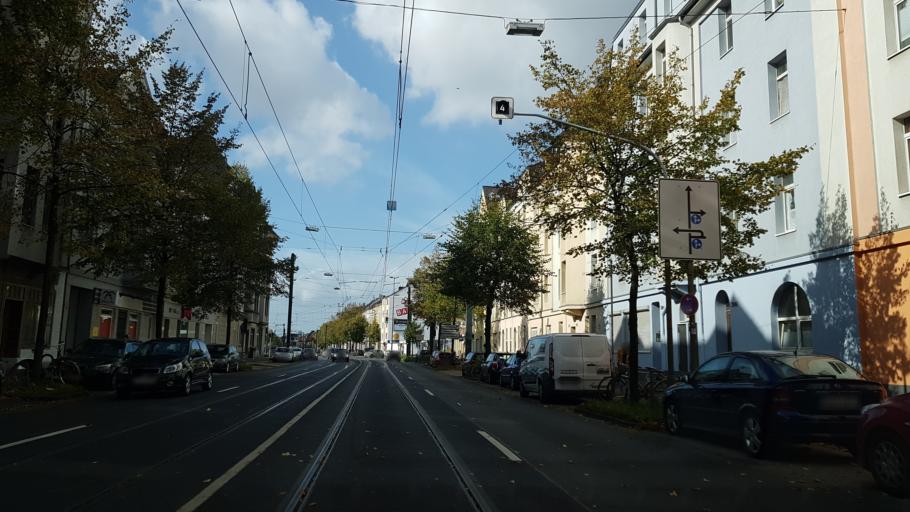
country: DE
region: North Rhine-Westphalia
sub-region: Regierungsbezirk Dusseldorf
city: Dusseldorf
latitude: 51.2158
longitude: 6.8204
